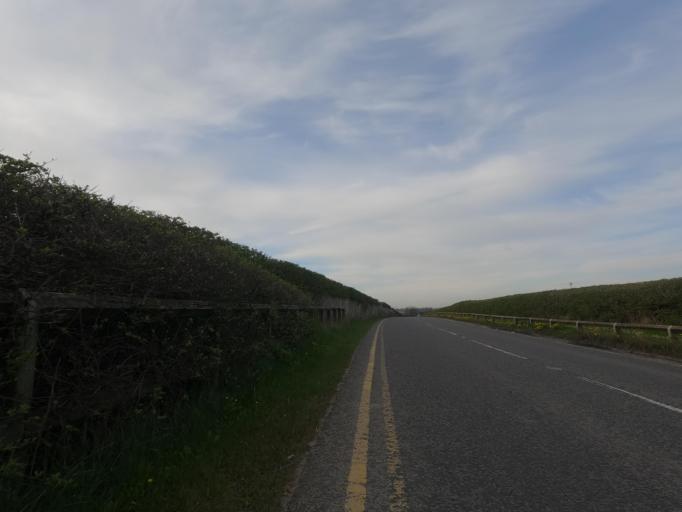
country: GB
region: England
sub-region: Newcastle upon Tyne
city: Dinnington
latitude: 55.0427
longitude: -1.6700
